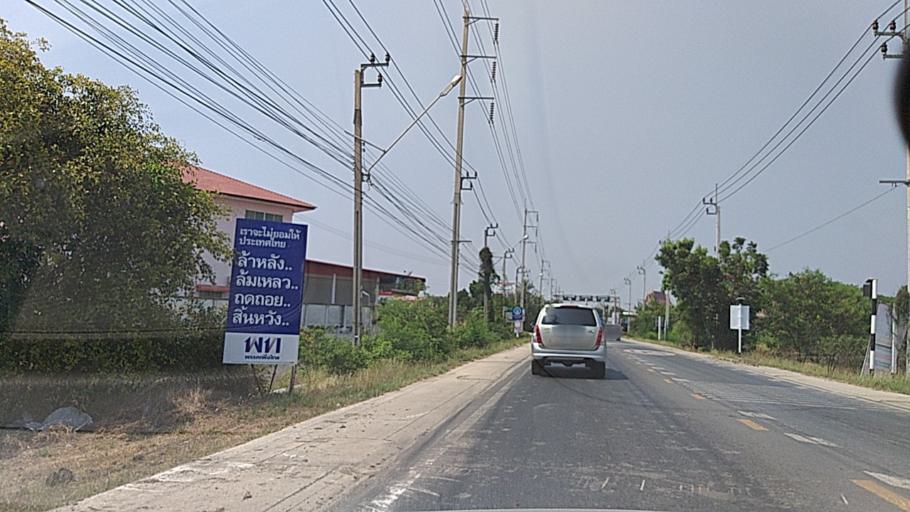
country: TH
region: Nonthaburi
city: Sai Noi
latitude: 13.9727
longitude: 100.3102
